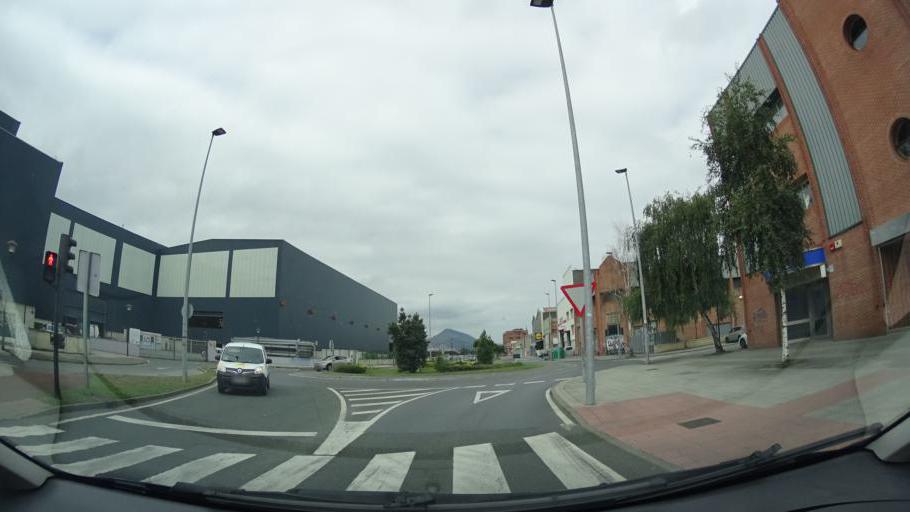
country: ES
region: Basque Country
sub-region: Bizkaia
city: Leioa
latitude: 43.3137
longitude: -2.9867
